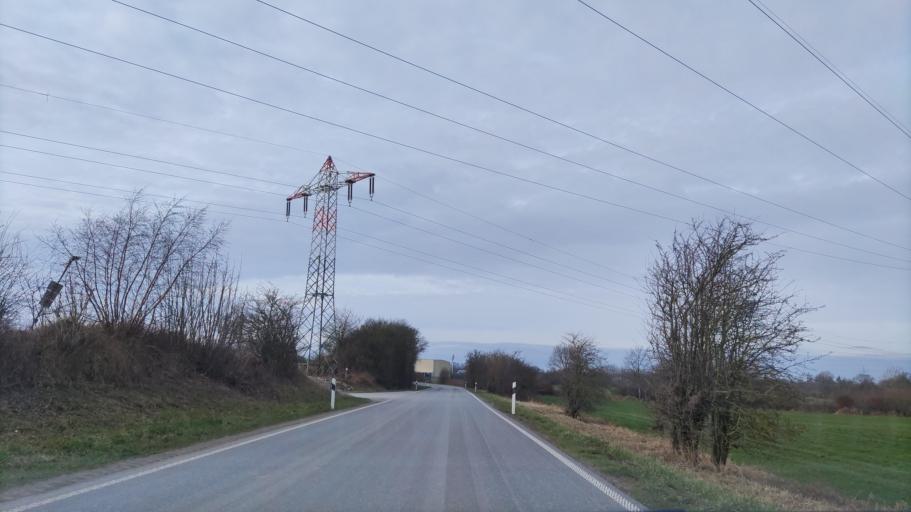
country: DE
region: Schleswig-Holstein
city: Selk
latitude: 54.4779
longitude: 9.5565
